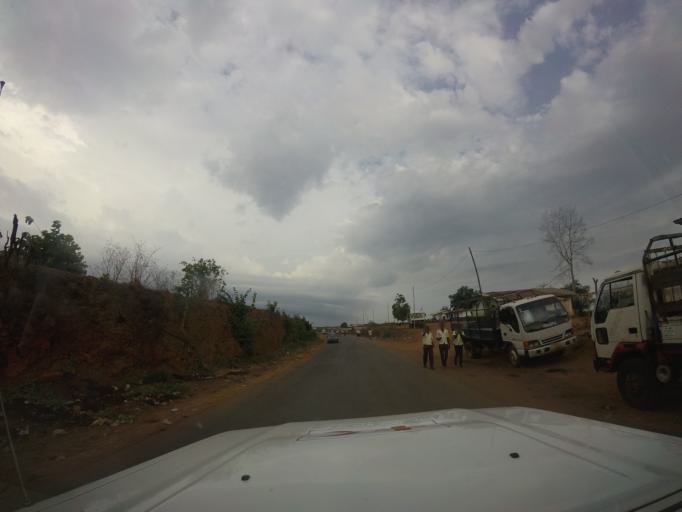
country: LR
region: Bomi
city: Tubmanburg
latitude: 6.7130
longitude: -10.9696
